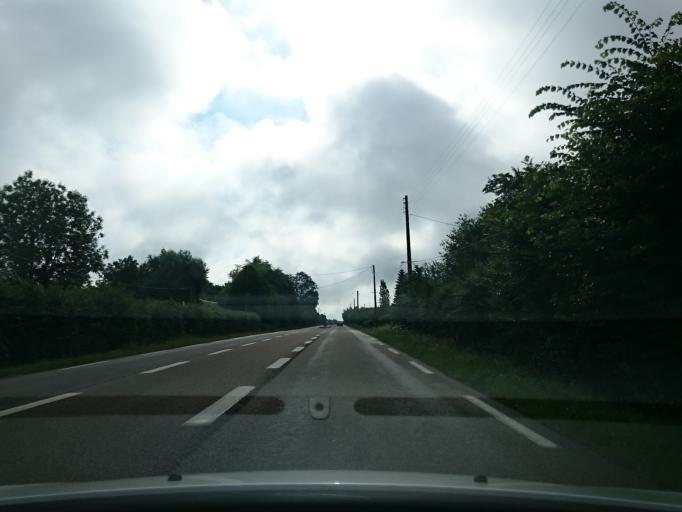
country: FR
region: Lower Normandy
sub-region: Departement du Calvados
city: Saint-Desir
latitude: 49.1352
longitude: 0.1418
